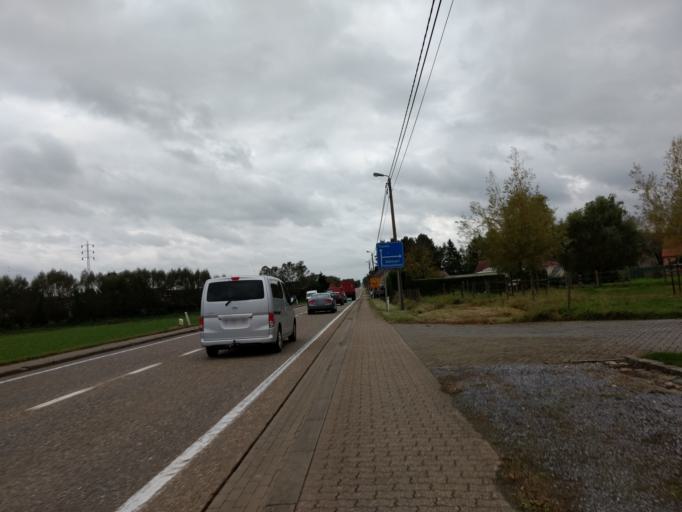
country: BE
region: Flanders
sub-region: Provincie Vlaams-Brabant
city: Bekkevoort
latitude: 50.9298
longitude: 4.9872
